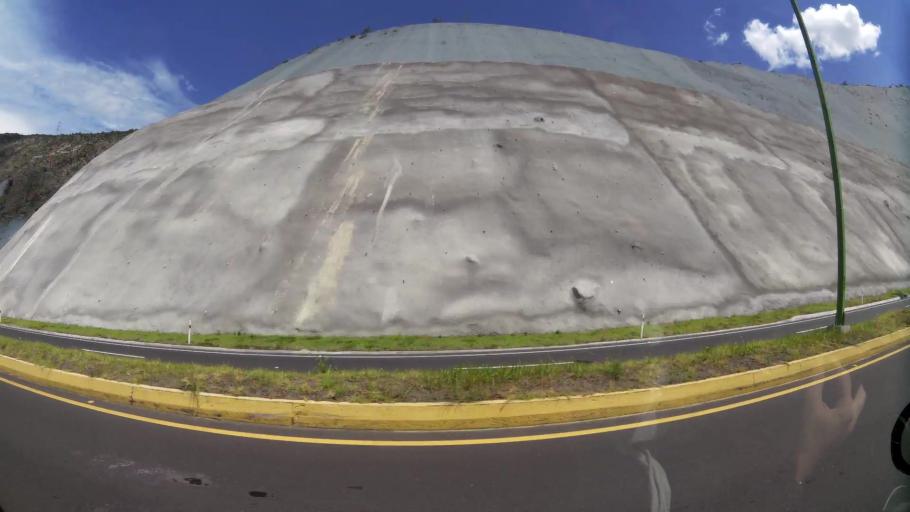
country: EC
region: Pichincha
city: Quito
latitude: -0.0986
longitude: -78.3891
